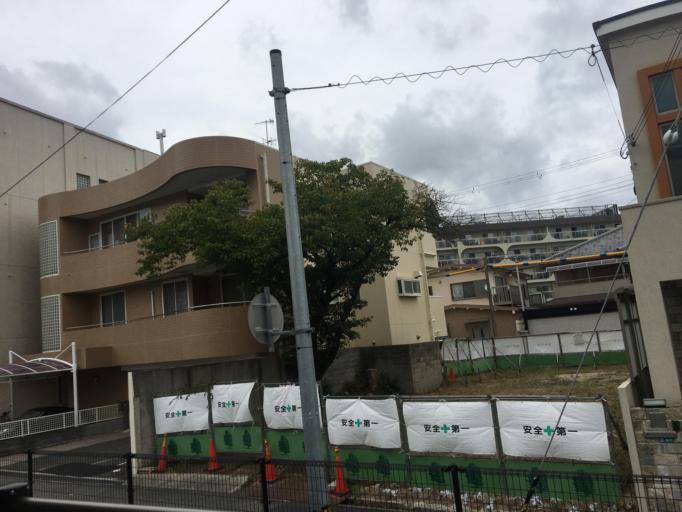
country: JP
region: Hyogo
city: Ashiya
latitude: 34.7606
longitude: 135.3307
